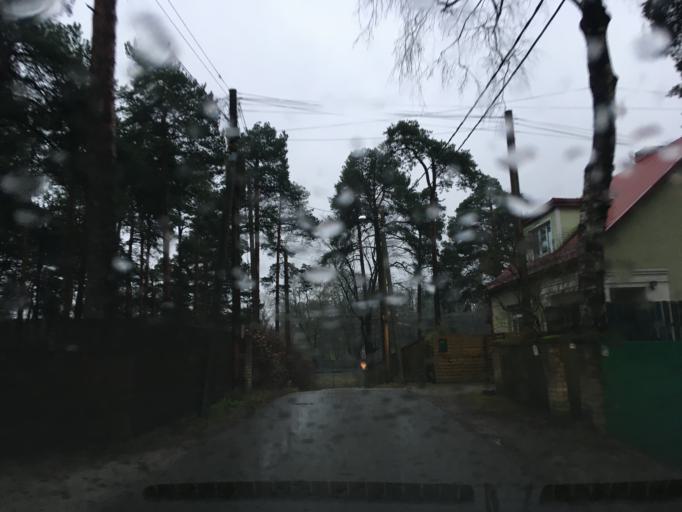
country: EE
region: Harju
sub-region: Tallinna linn
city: Tallinn
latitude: 59.3882
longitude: 24.6948
